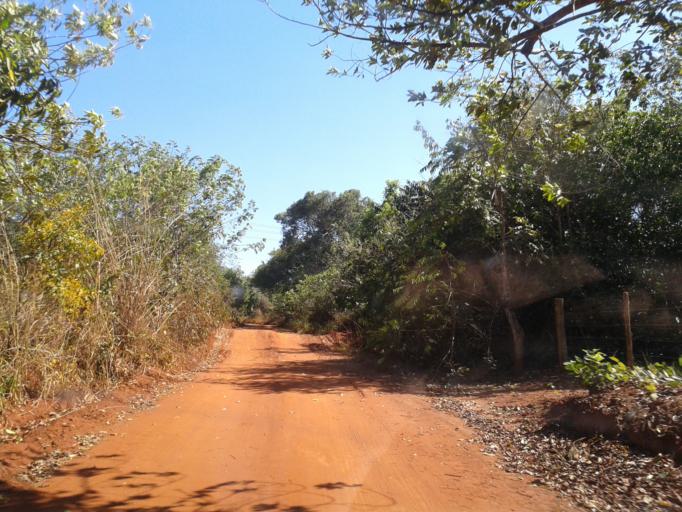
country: BR
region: Minas Gerais
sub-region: Monte Alegre De Minas
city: Monte Alegre de Minas
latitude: -18.8761
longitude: -49.1311
